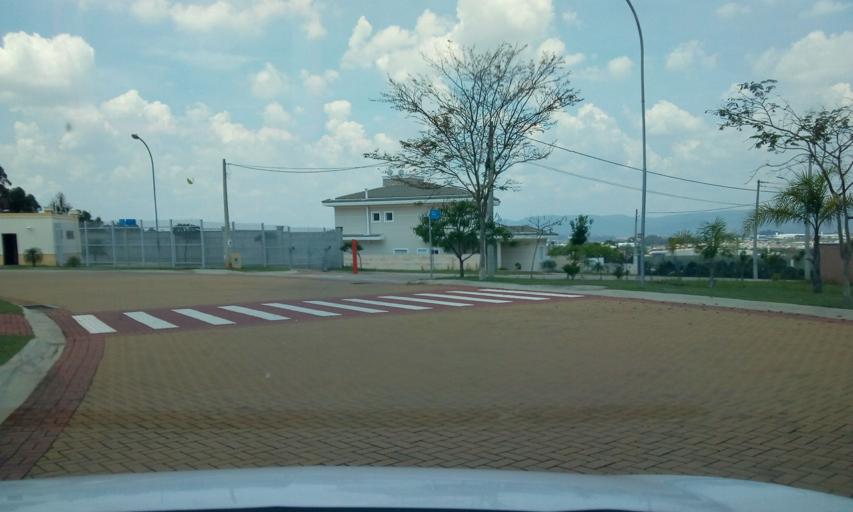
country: BR
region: Sao Paulo
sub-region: Itupeva
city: Itupeva
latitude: -23.1321
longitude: -47.0495
